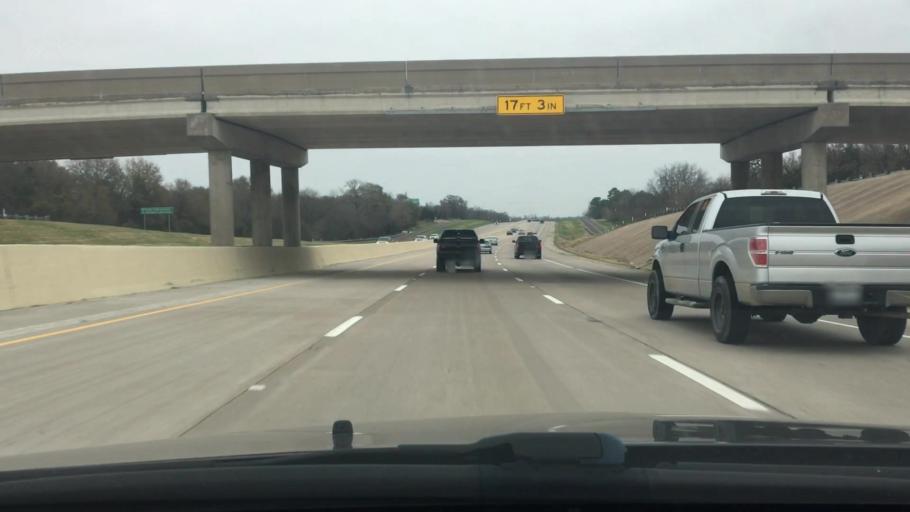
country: US
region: Texas
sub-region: Navarro County
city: Corsicana
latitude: 31.9636
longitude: -96.4206
